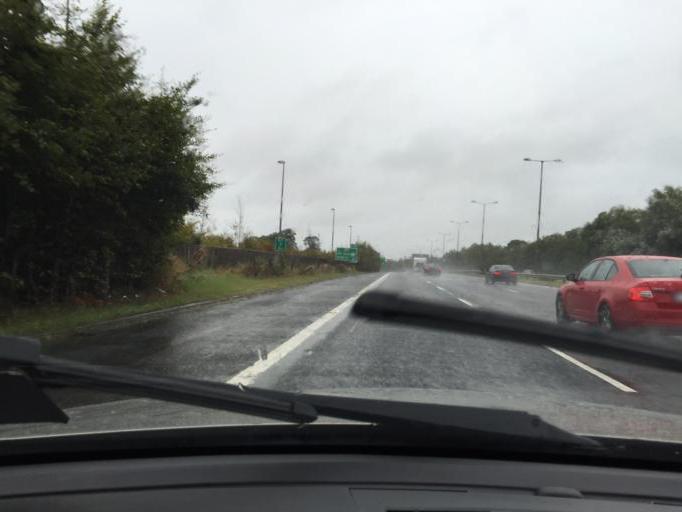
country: IE
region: Leinster
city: Clondalkin
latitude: 53.3051
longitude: -6.4115
